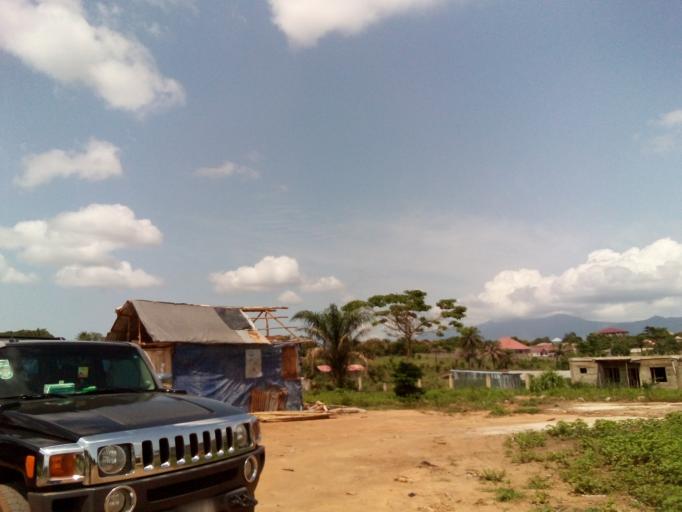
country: SL
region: Western Area
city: Waterloo
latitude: 8.3385
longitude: -13.0255
